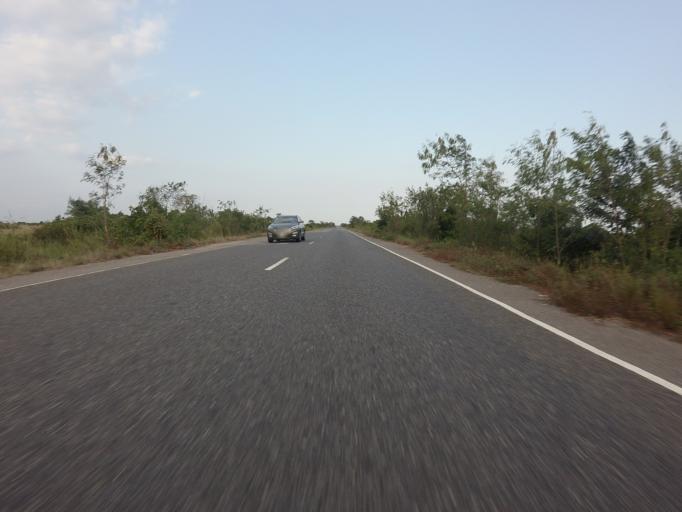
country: GH
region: Volta
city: Anloga
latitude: 6.0828
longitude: 0.5662
